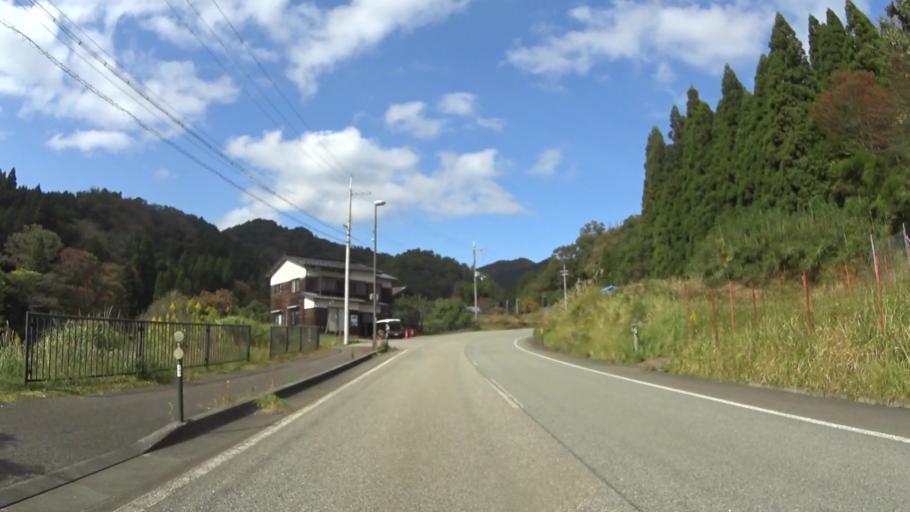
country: JP
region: Hyogo
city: Toyooka
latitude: 35.5115
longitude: 134.9919
